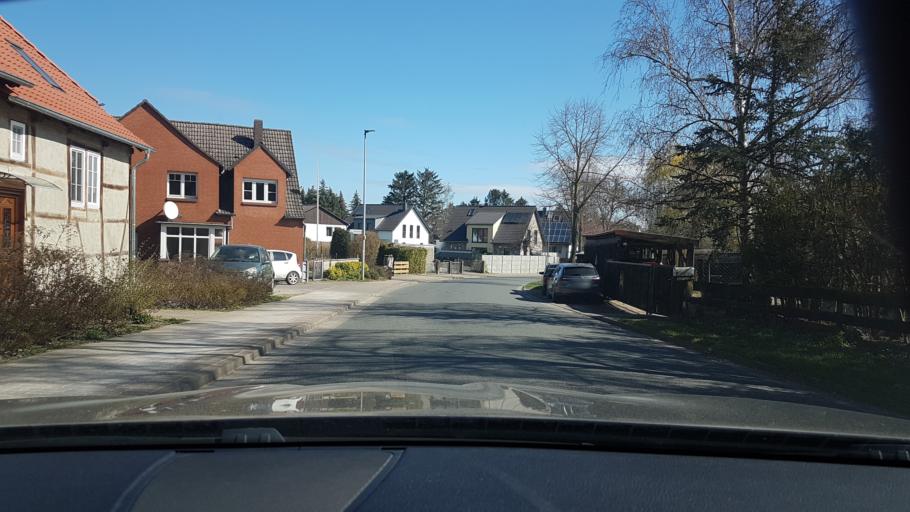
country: DE
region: Lower Saxony
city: Pattensen
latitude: 52.2179
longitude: 9.7056
